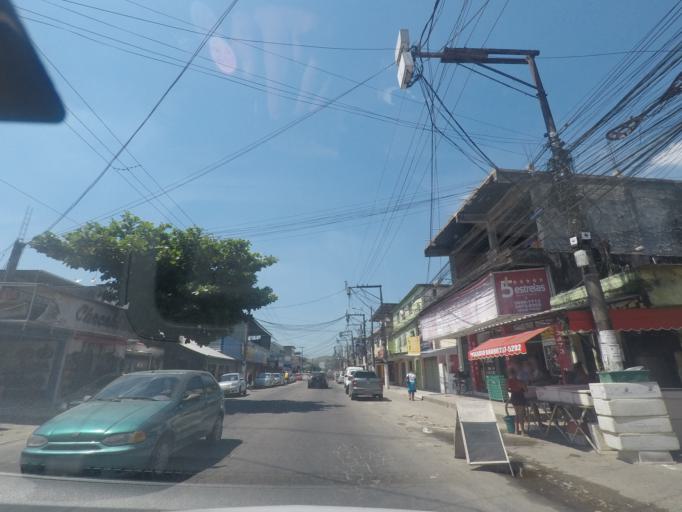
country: BR
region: Rio de Janeiro
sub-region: Petropolis
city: Petropolis
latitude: -22.5895
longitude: -43.1863
